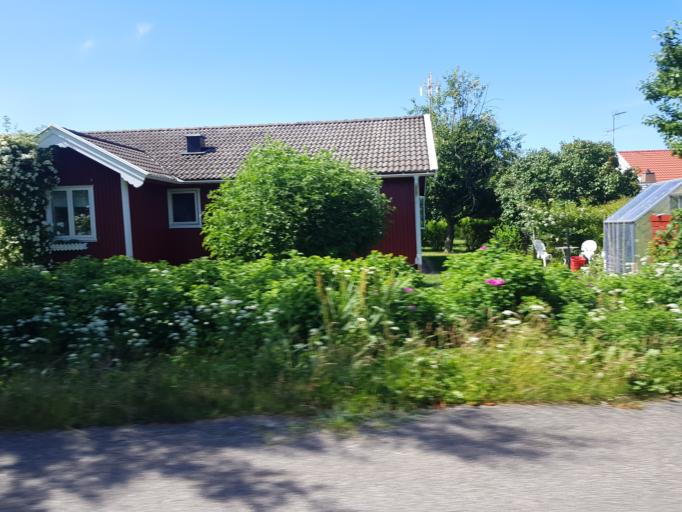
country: SE
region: Vaestra Goetaland
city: Ronnang
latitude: 57.9407
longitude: 11.5972
